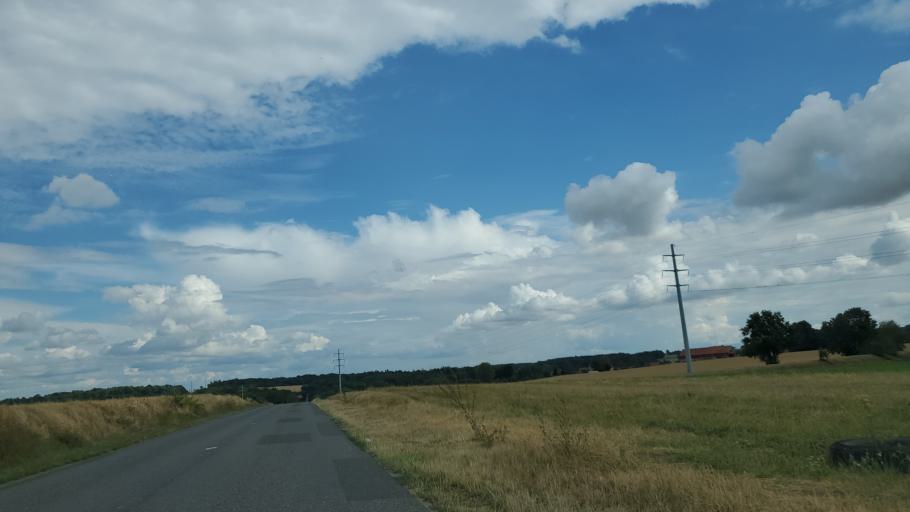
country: FR
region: Ile-de-France
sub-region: Departement de Seine-et-Marne
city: Chailly-en-Brie
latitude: 48.7828
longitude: 3.1559
